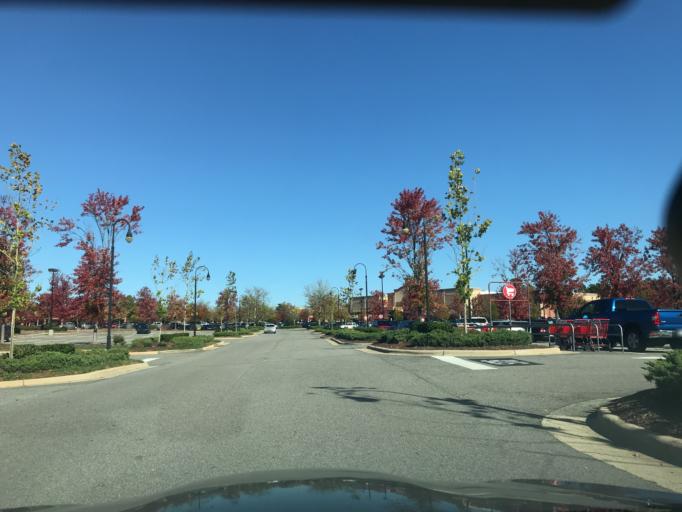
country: US
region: North Carolina
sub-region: Wake County
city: Morrisville
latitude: 35.9032
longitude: -78.7866
